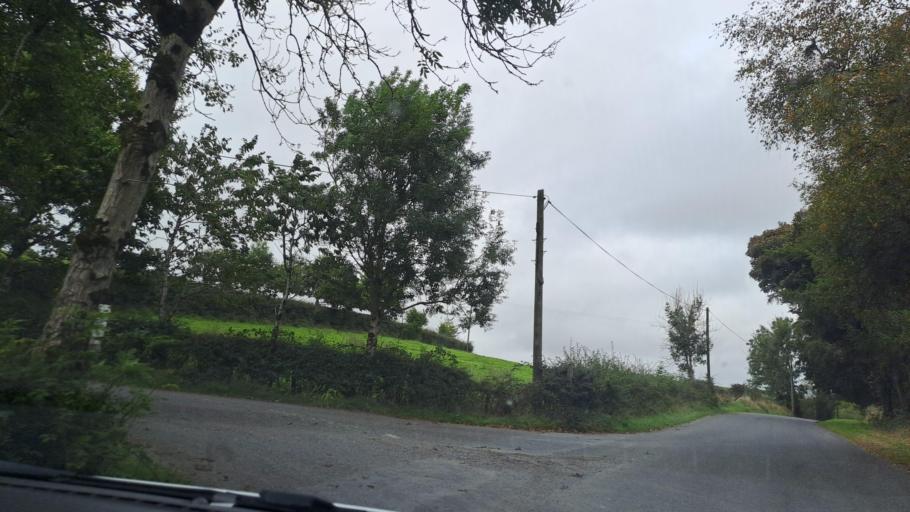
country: IE
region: Ulster
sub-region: County Monaghan
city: Carrickmacross
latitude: 54.0336
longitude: -6.7619
